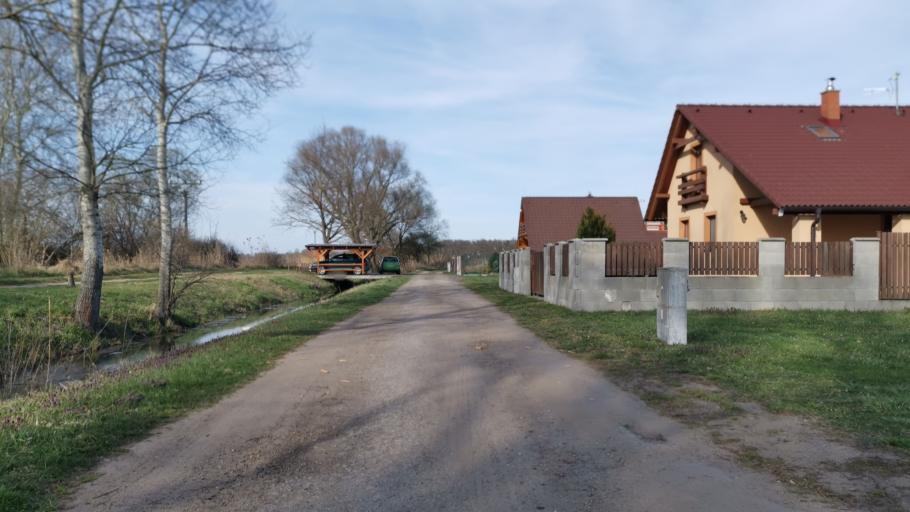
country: CZ
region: South Moravian
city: Tvrdonice
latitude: 48.7302
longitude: 17.0405
